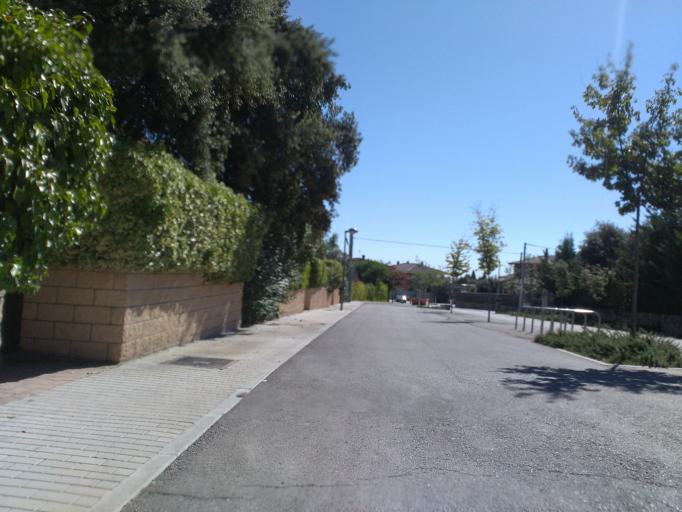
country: ES
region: Madrid
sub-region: Provincia de Madrid
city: Torrelodones
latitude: 40.5808
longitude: -3.9349
